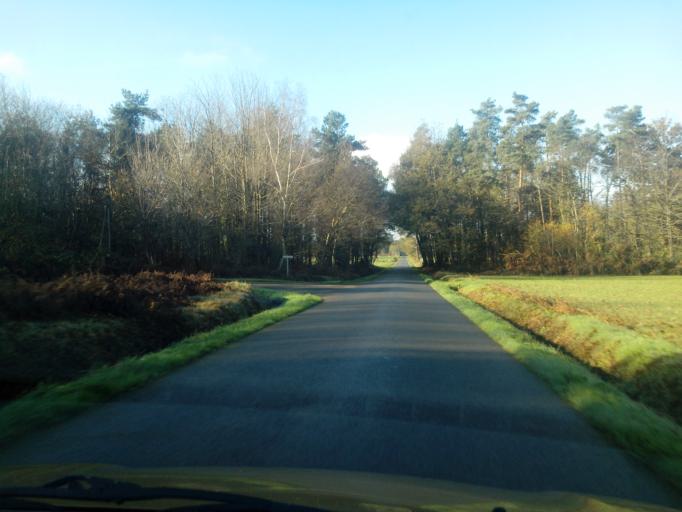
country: FR
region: Brittany
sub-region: Departement du Morbihan
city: Pleucadeuc
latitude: 47.7270
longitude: -2.3913
